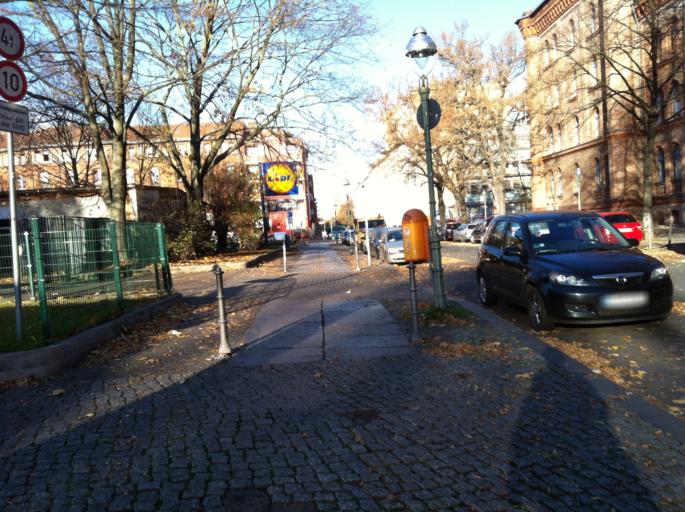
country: DE
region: Berlin
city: Berlin Treptow
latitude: 52.5009
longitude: 13.4361
